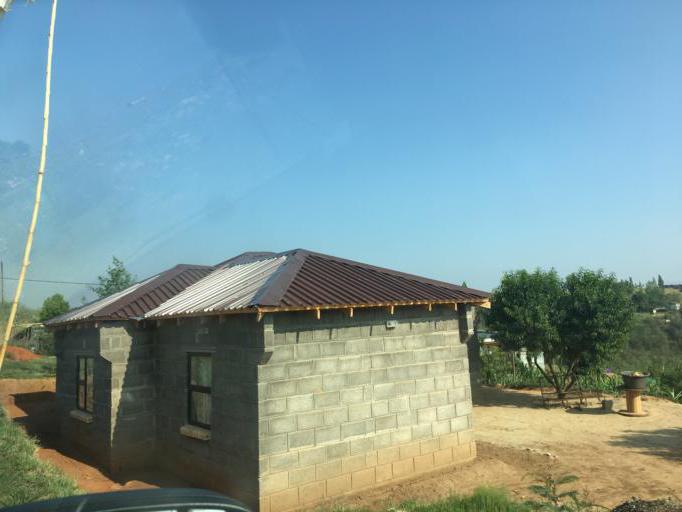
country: LS
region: Maseru
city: Maseru
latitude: -29.4483
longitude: 27.5642
